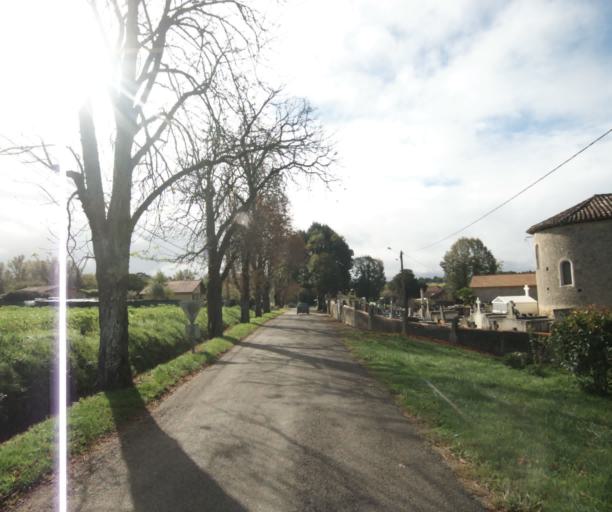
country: FR
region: Midi-Pyrenees
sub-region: Departement du Gers
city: Cazaubon
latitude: 43.8650
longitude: -0.0730
